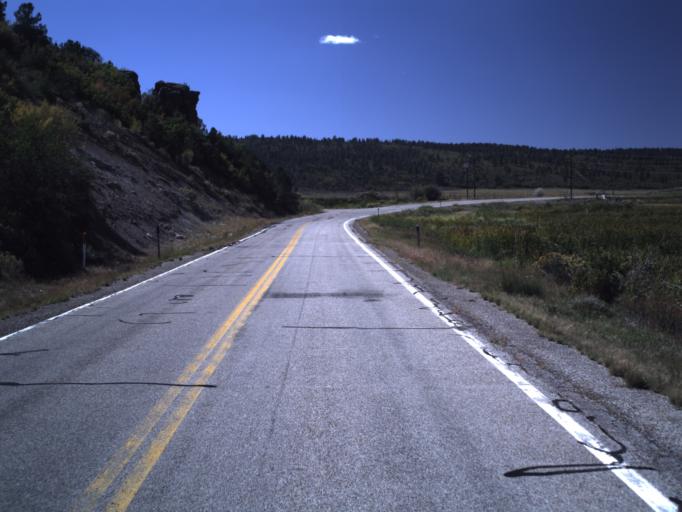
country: US
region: Utah
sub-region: Grand County
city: Moab
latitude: 38.3273
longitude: -109.1212
